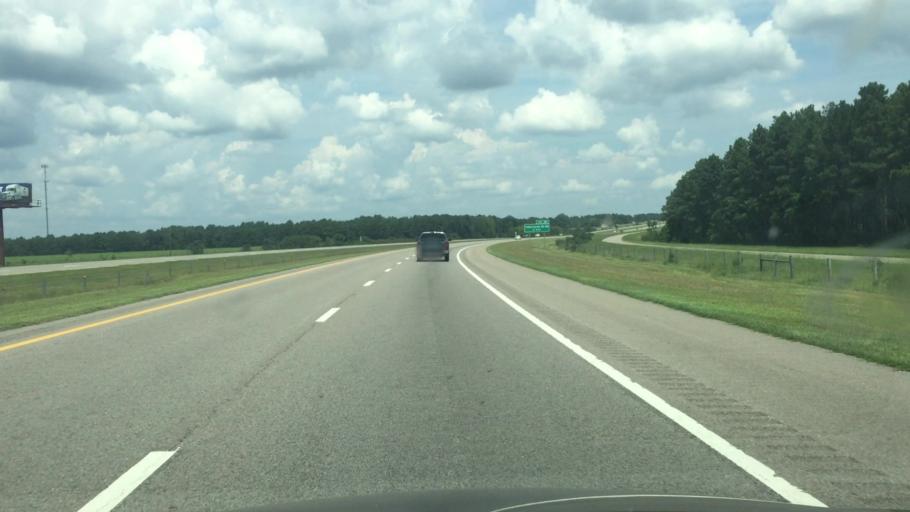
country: US
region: North Carolina
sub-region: Richmond County
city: Ellerbe
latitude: 35.1924
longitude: -79.7260
